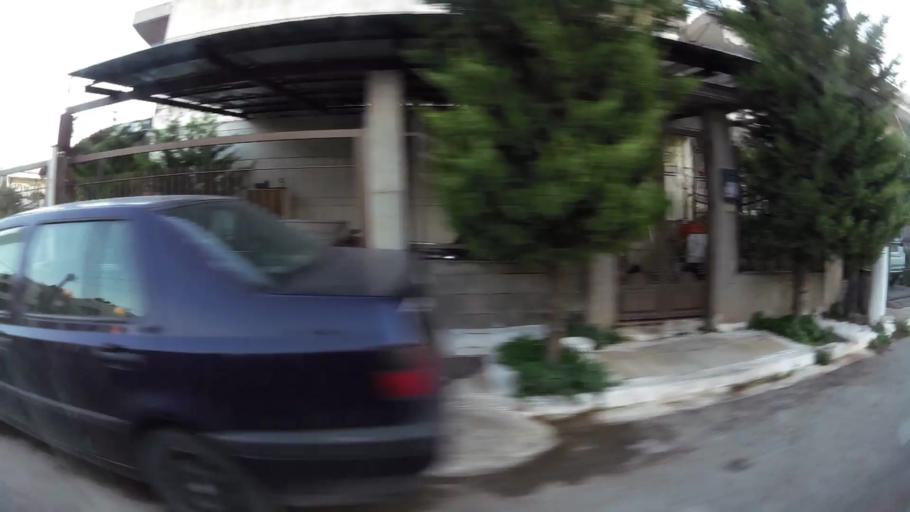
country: GR
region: Attica
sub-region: Nomarchia Dytikis Attikis
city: Ano Liosia
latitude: 38.0836
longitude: 23.7016
